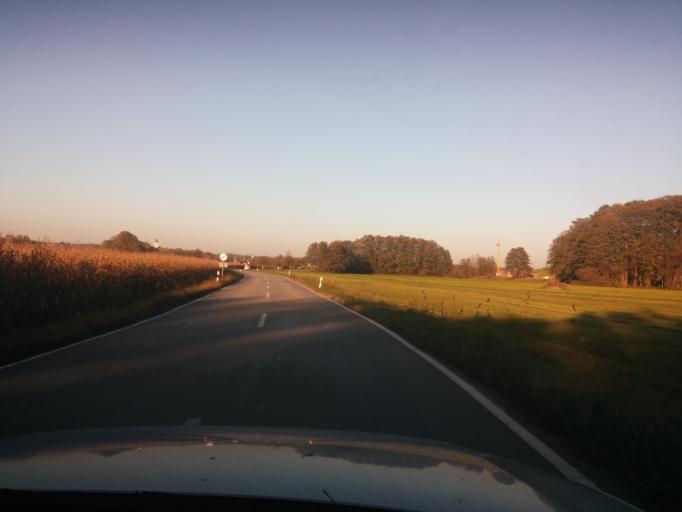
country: DE
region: Bavaria
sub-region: Upper Bavaria
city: Dorfen
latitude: 48.2589
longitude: 12.1365
